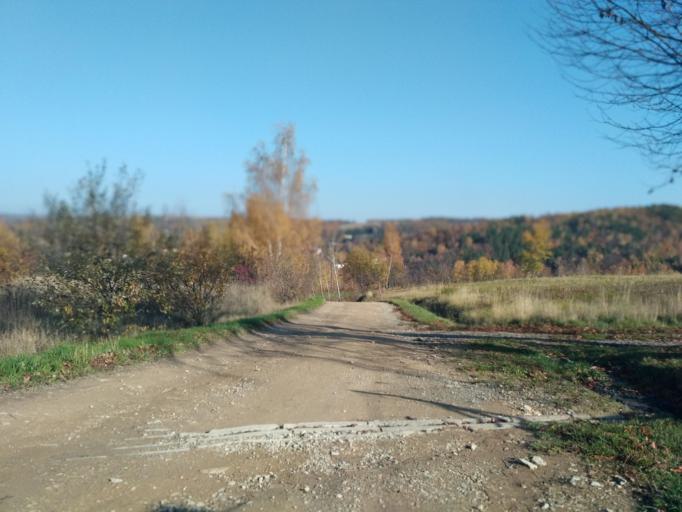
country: PL
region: Subcarpathian Voivodeship
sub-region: Powiat rzeszowski
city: Blazowa
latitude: 49.8759
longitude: 22.0920
